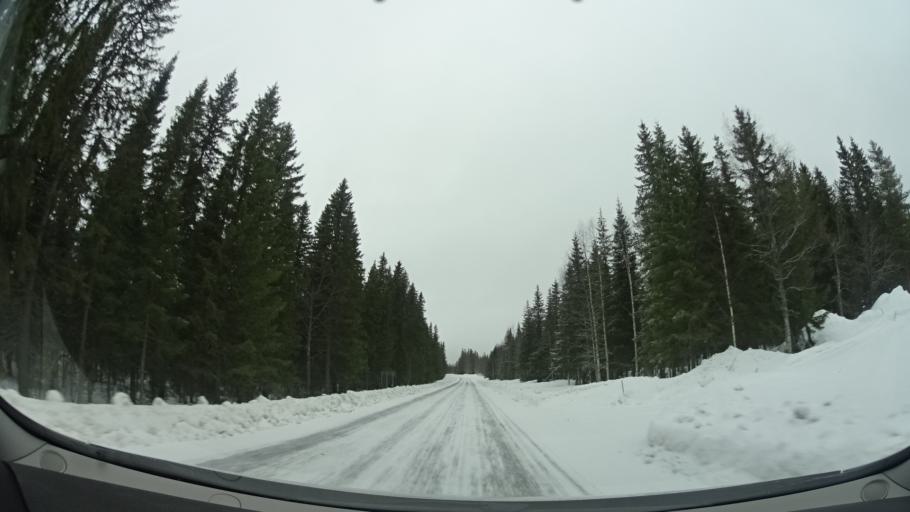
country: SE
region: Vaesterbotten
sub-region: Mala Kommun
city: Mala
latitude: 65.0969
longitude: 18.9220
